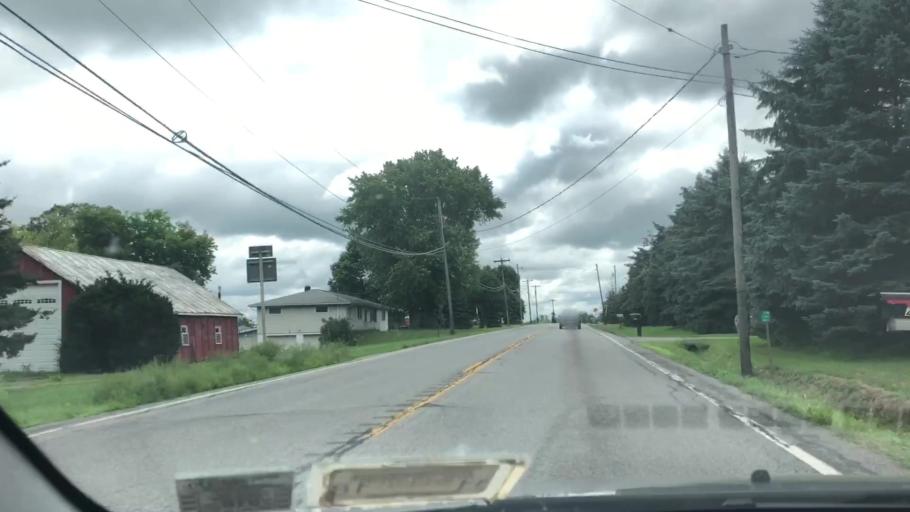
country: US
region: New York
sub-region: Wayne County
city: Macedon
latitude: 43.1100
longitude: -77.2928
